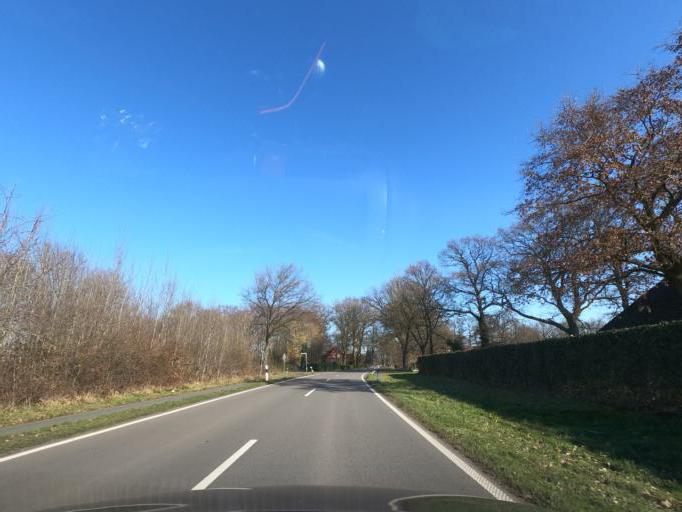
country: DE
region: Lower Saxony
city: Cappeln
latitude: 52.8573
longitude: 8.0979
